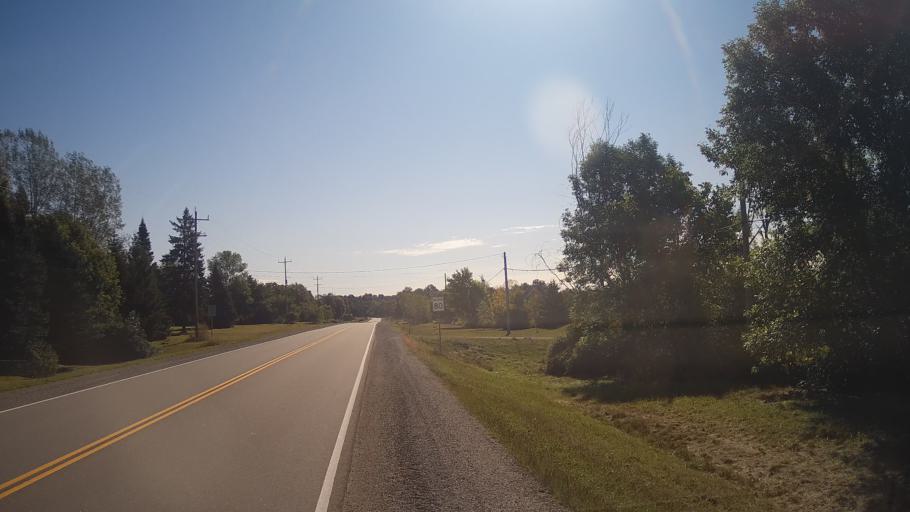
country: CA
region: Ontario
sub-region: Lanark County
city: Smiths Falls
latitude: 44.6259
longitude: -76.0001
